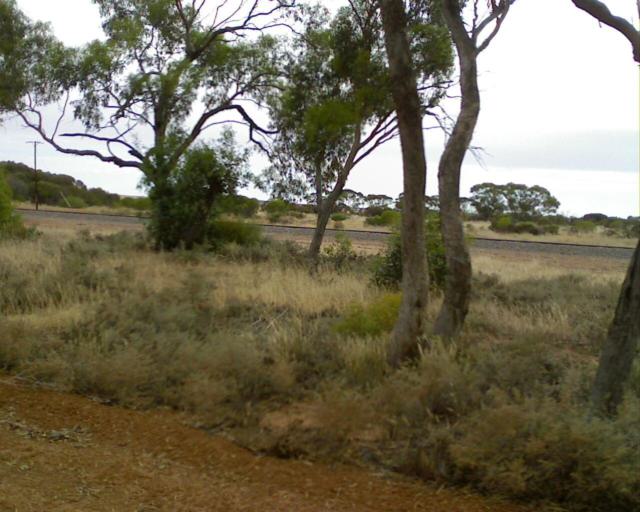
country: AU
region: Western Australia
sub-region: Moora
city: Moora
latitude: -29.7711
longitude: 115.9268
